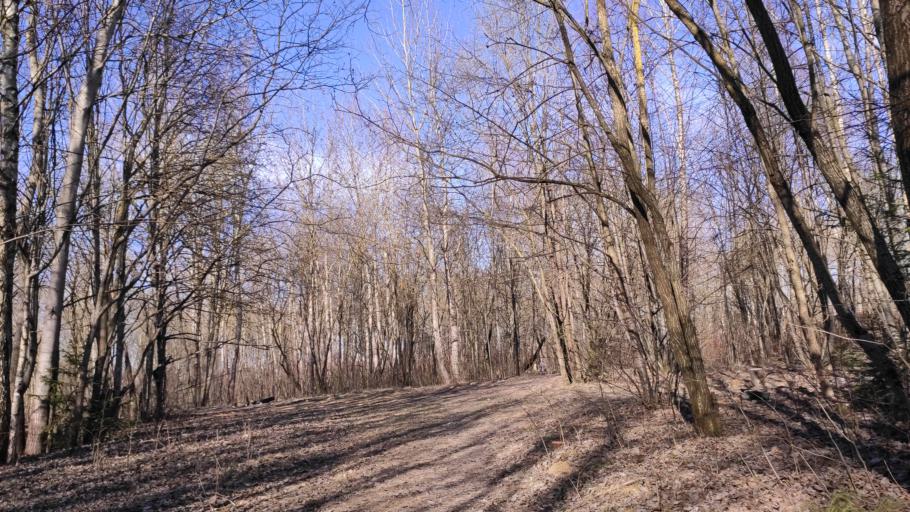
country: BY
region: Minsk
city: Novoye Medvezhino
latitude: 53.8898
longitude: 27.4596
